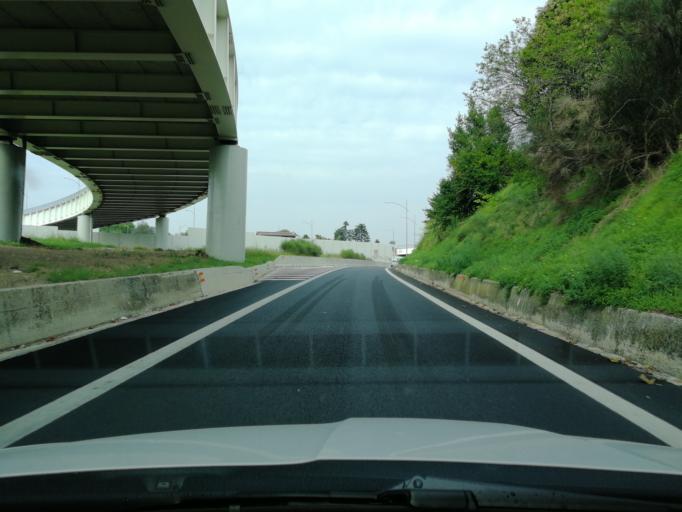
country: IT
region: Latium
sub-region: Citta metropolitana di Roma Capitale
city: Setteville
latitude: 41.9204
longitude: 12.6132
